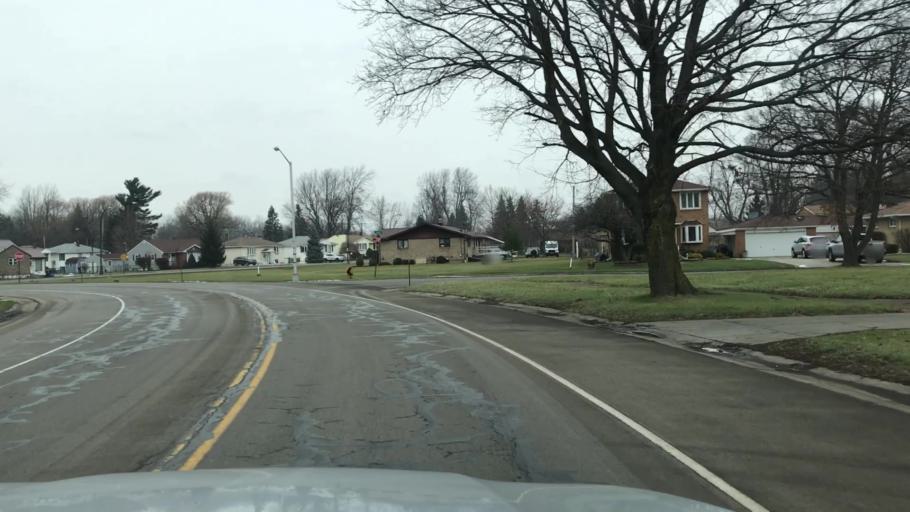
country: US
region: New York
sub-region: Erie County
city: Lackawanna
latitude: 42.8189
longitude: -78.8090
